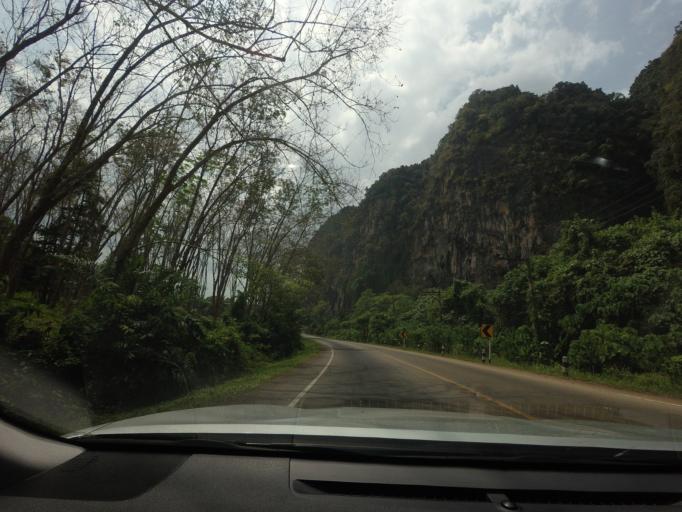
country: TH
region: Phangnga
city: Ban Ao Nang
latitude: 8.1358
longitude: 98.8073
